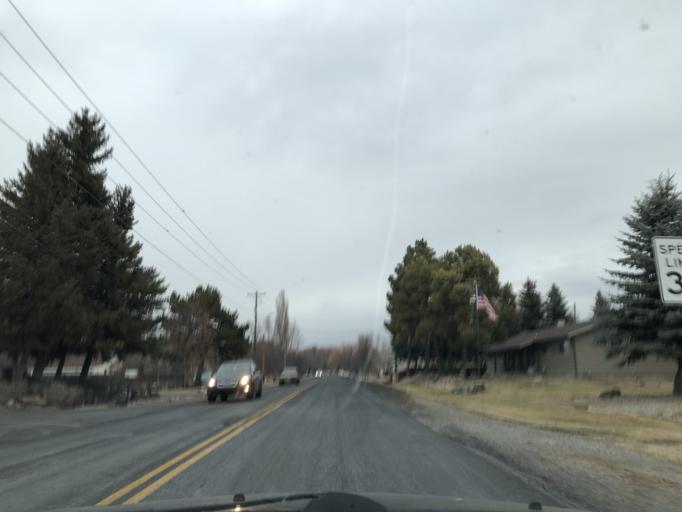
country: US
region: Utah
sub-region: Cache County
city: Logan
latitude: 41.7144
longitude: -111.8528
